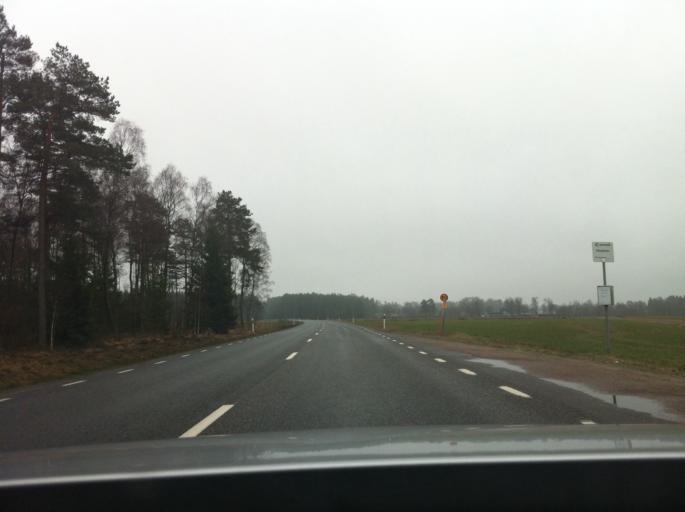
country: SE
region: Vaestra Goetaland
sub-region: Svenljunga Kommun
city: Svenljunga
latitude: 57.4725
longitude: 13.1108
